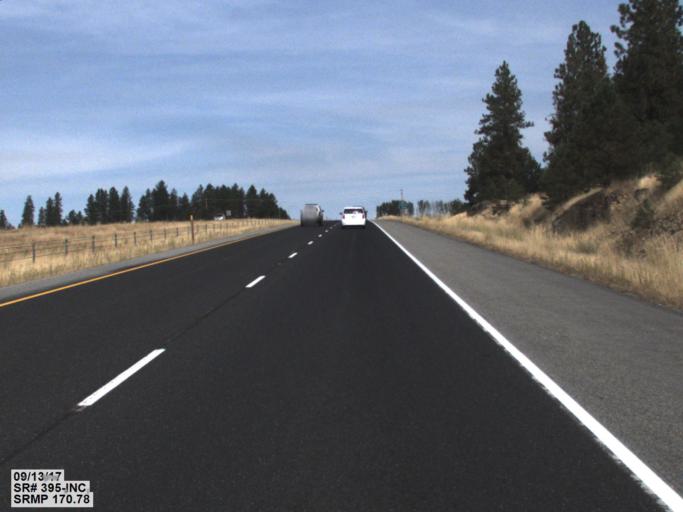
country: US
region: Washington
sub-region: Spokane County
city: Fairwood
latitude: 47.8272
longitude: -117.4164
